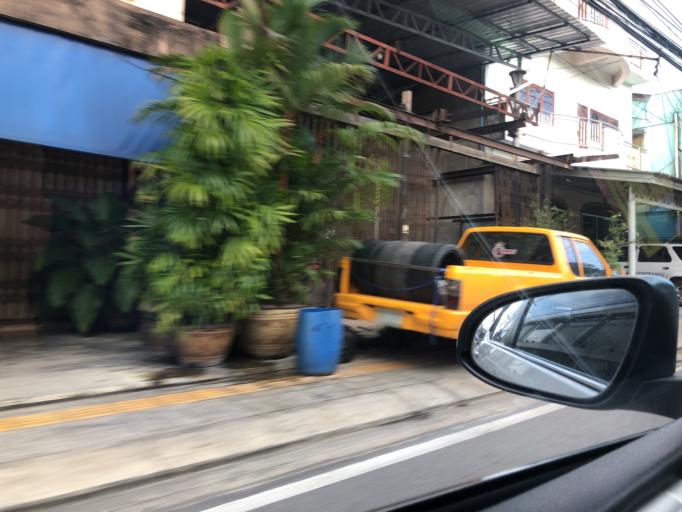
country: TH
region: Phuket
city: Wichit
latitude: 7.8948
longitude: 98.3895
